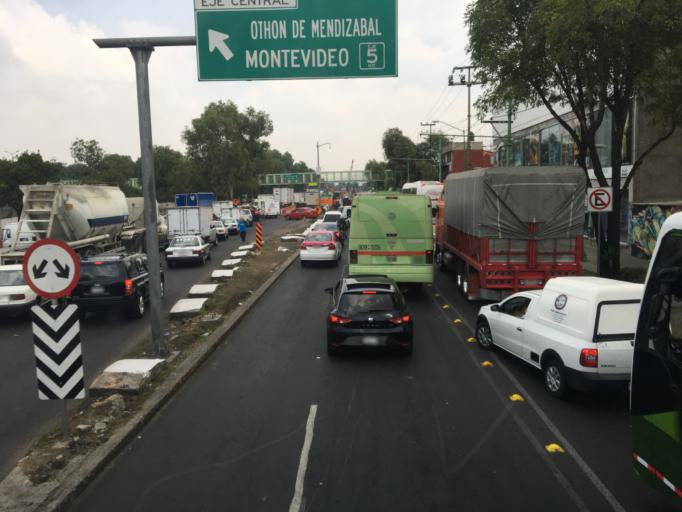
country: MX
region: Mexico
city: Colonia Lindavista
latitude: 19.4905
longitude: -99.1448
